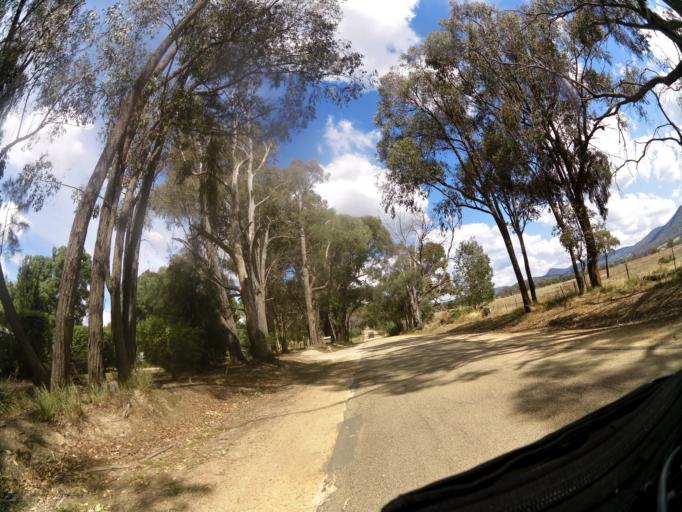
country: AU
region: Victoria
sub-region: Benalla
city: Benalla
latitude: -36.7719
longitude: 145.9748
